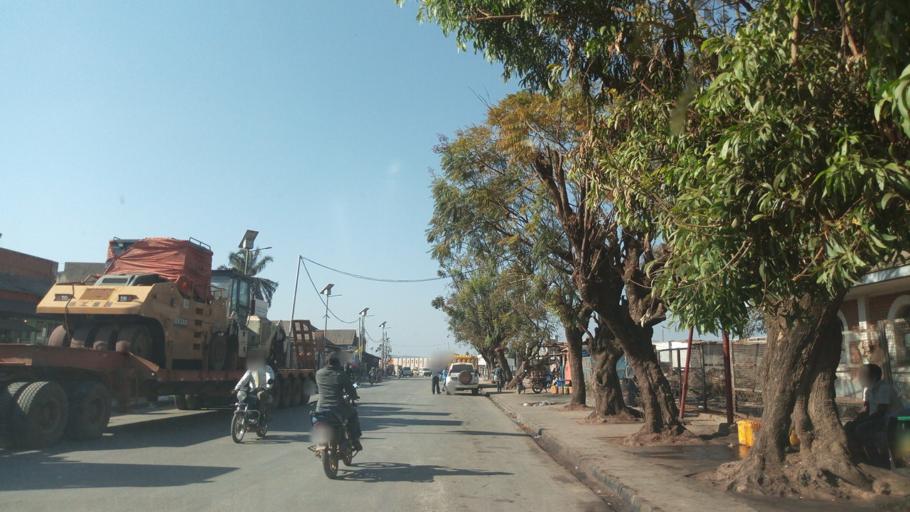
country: CD
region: Katanga
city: Likasi
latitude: -10.9868
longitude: 26.7431
